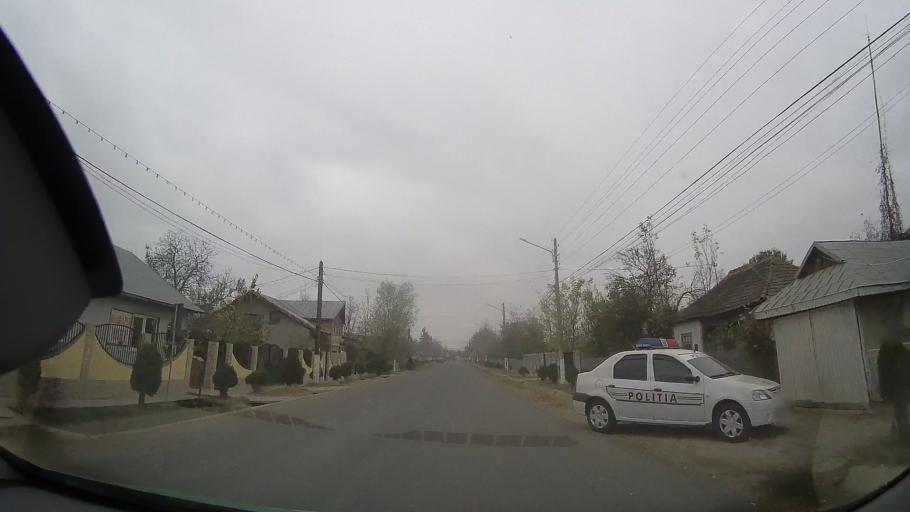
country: RO
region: Braila
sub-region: Comuna Ciocile
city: Ciocile
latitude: 44.8210
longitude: 27.2501
